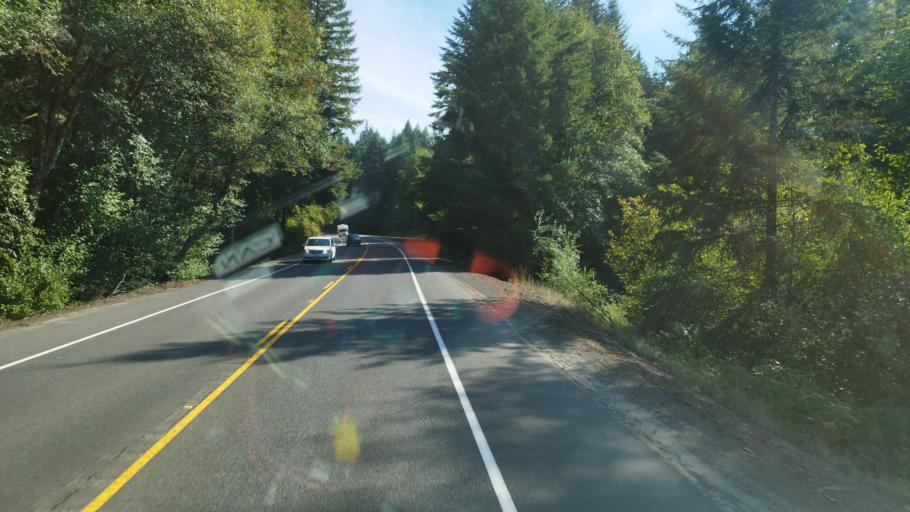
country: US
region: Oregon
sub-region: Columbia County
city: Vernonia
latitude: 45.7652
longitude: -123.3161
